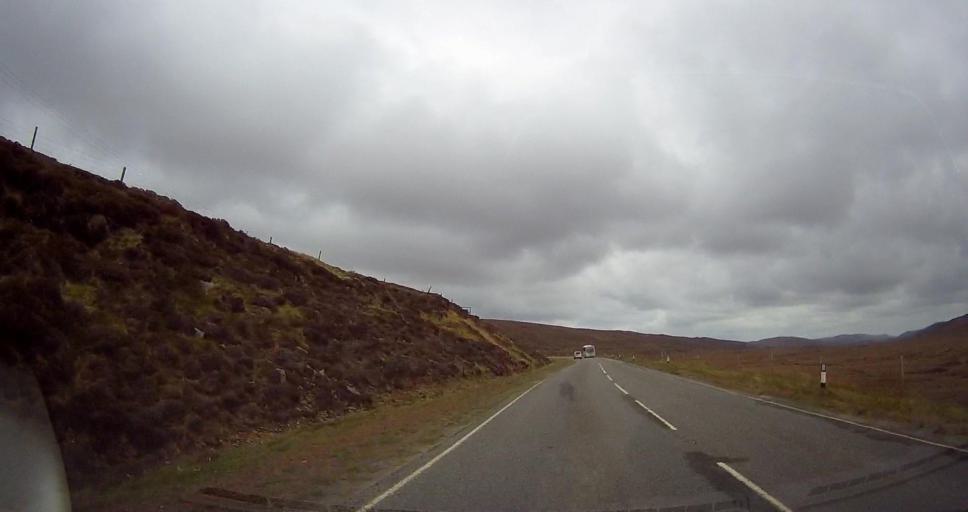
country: GB
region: Scotland
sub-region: Shetland Islands
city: Lerwick
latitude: 60.3106
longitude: -1.2461
